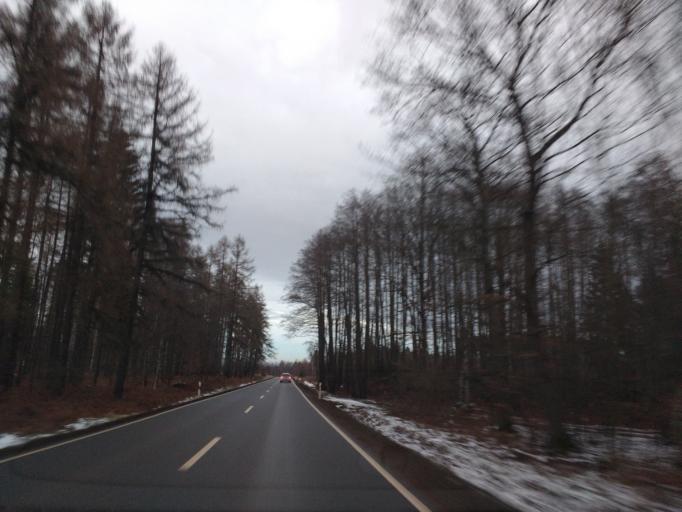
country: DE
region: Saxony-Anhalt
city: Friedrichsbrunn
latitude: 51.7034
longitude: 11.0667
